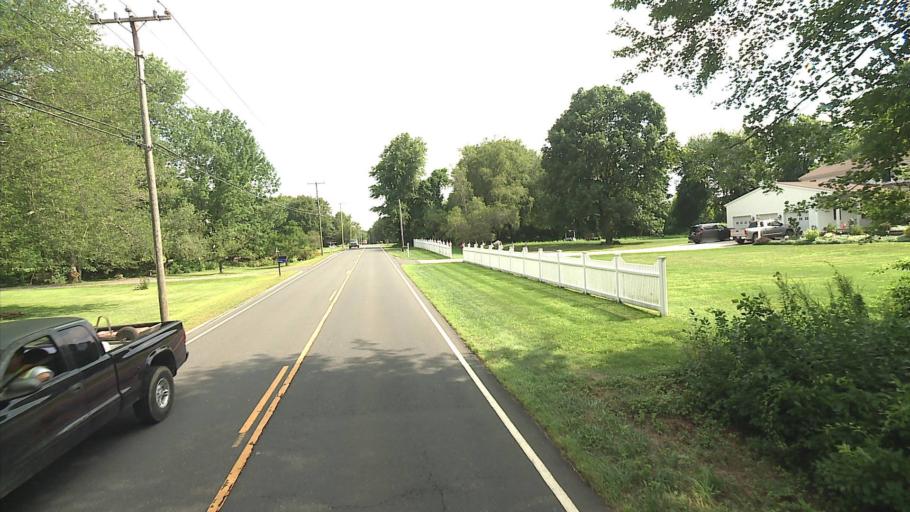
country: US
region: Connecticut
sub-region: Middlesex County
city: Moodus
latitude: 41.5315
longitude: -72.4119
